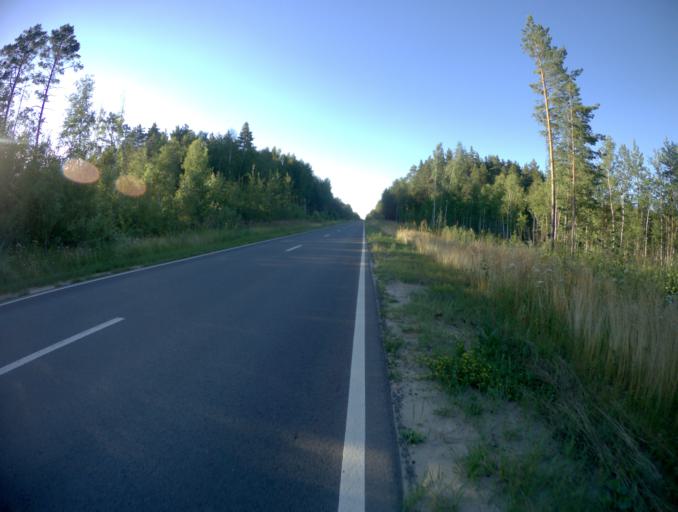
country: RU
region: Vladimir
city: Galitsy
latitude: 56.0704
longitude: 42.8669
